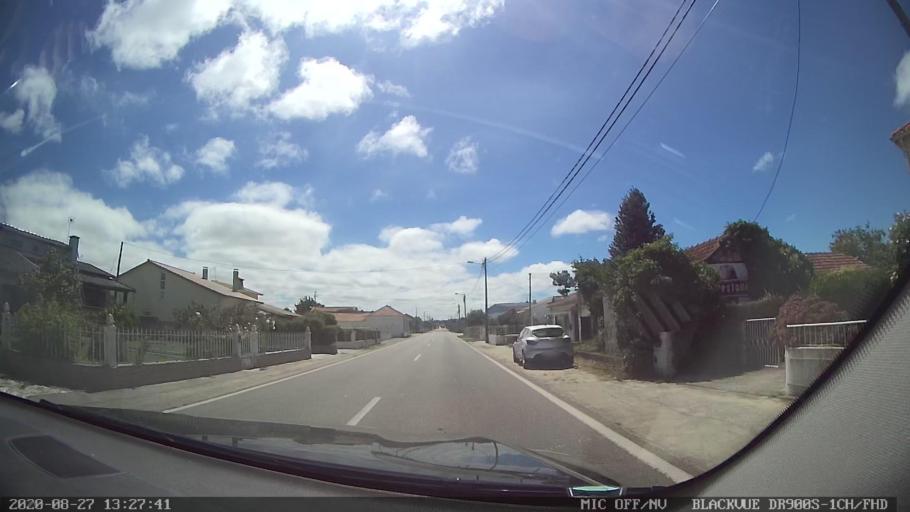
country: PT
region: Aveiro
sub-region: Vagos
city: Vagos
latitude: 40.5283
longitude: -8.6791
